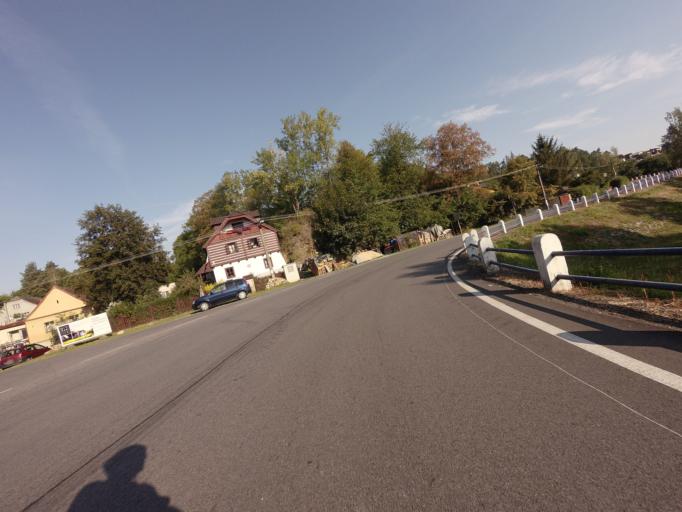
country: CZ
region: Jihocesky
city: Tyn nad Vltavou
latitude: 49.2530
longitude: 14.4197
